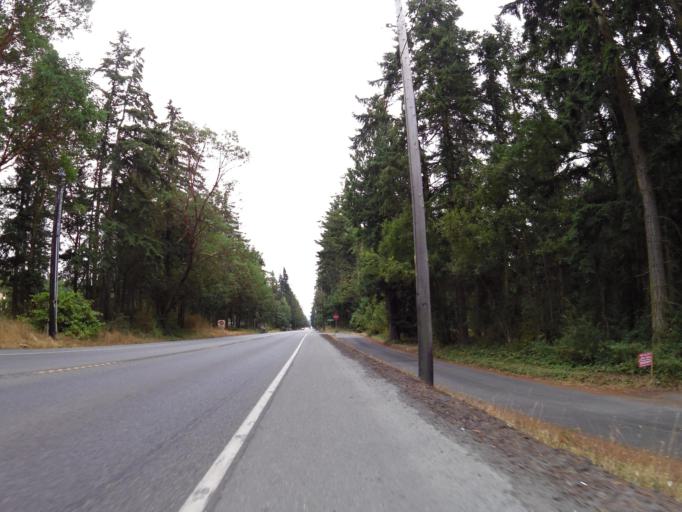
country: US
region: Washington
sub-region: Jefferson County
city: Port Hadlock-Irondale
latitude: 48.0658
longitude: -122.8132
